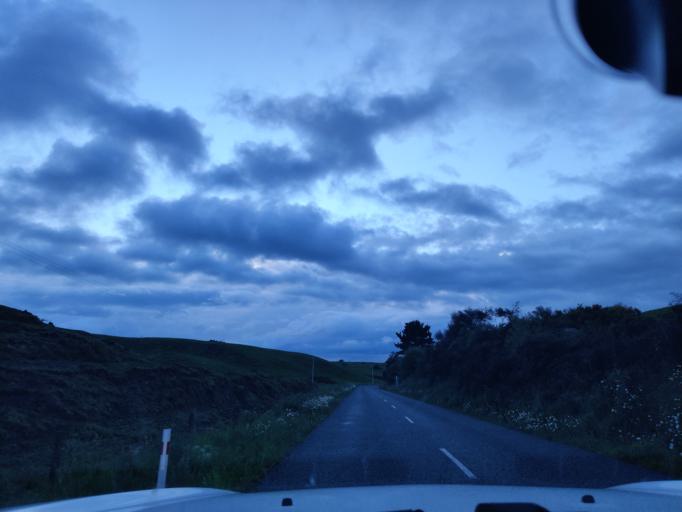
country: NZ
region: Waikato
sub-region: South Waikato District
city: Tokoroa
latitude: -38.1786
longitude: 175.7791
